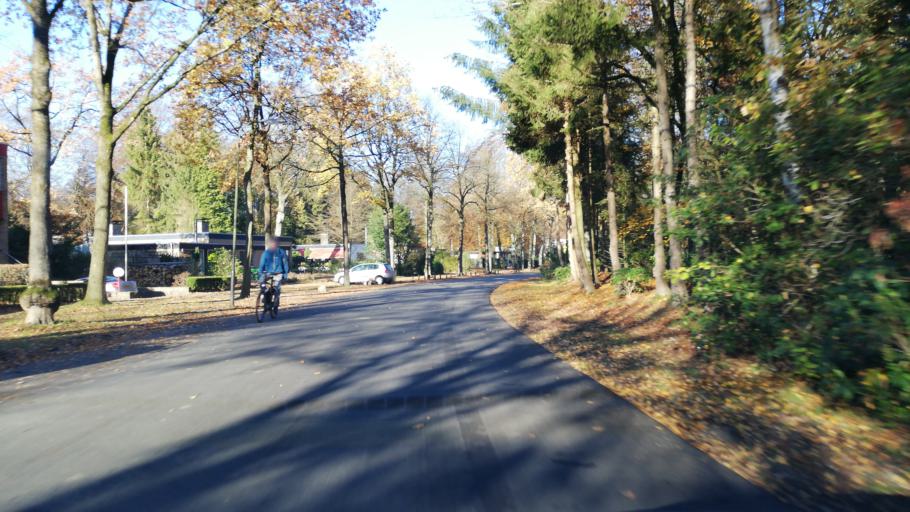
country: NL
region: Gelderland
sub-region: Gemeente Apeldoorn
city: Apeldoorn
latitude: 52.2188
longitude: 5.9289
